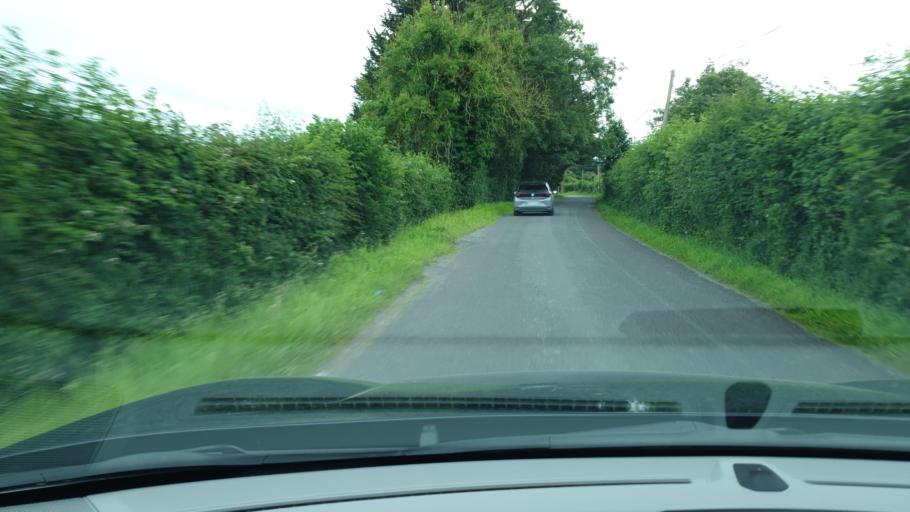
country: IE
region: Leinster
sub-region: An Mhi
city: Dunshaughlin
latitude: 53.5221
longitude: -6.5276
